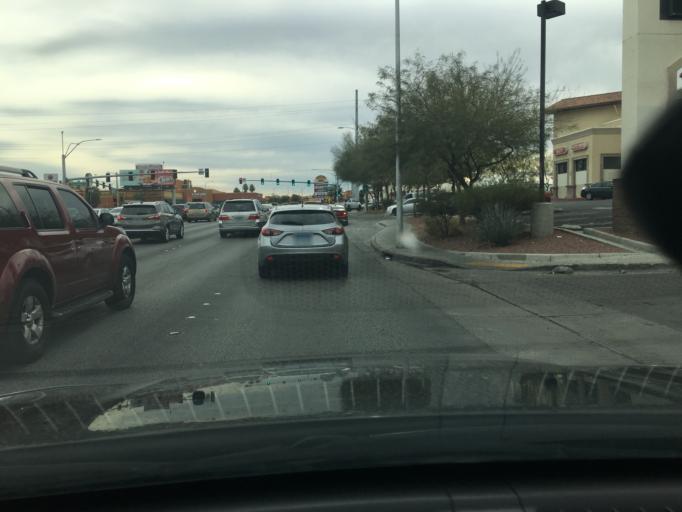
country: US
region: Nevada
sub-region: Clark County
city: Spring Valley
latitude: 36.1601
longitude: -115.2061
